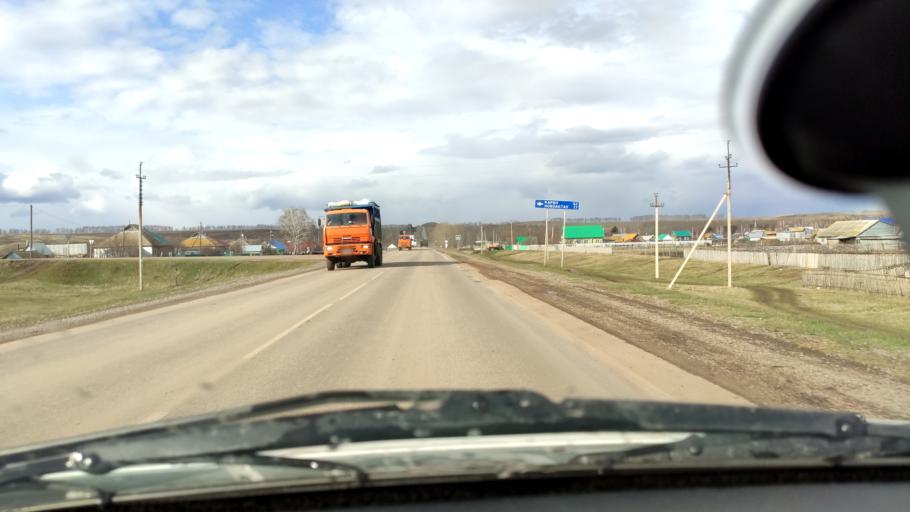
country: RU
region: Bashkortostan
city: Buzdyak
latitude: 54.6829
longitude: 54.5529
